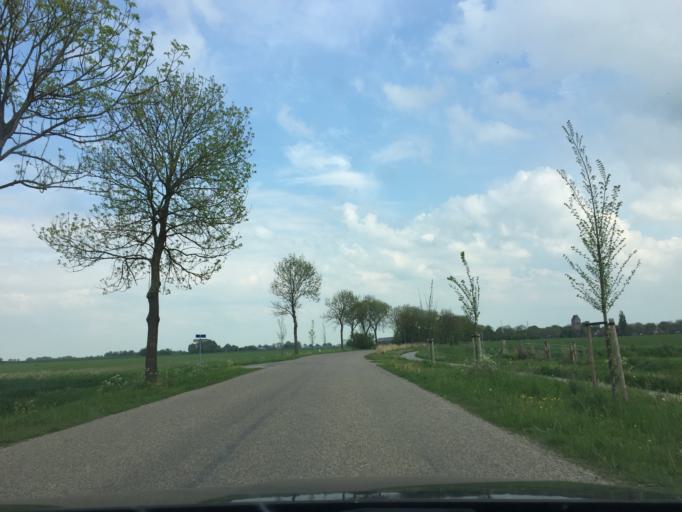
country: NL
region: Groningen
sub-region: Gemeente Zuidhorn
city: Oldehove
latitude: 53.3072
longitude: 6.3818
